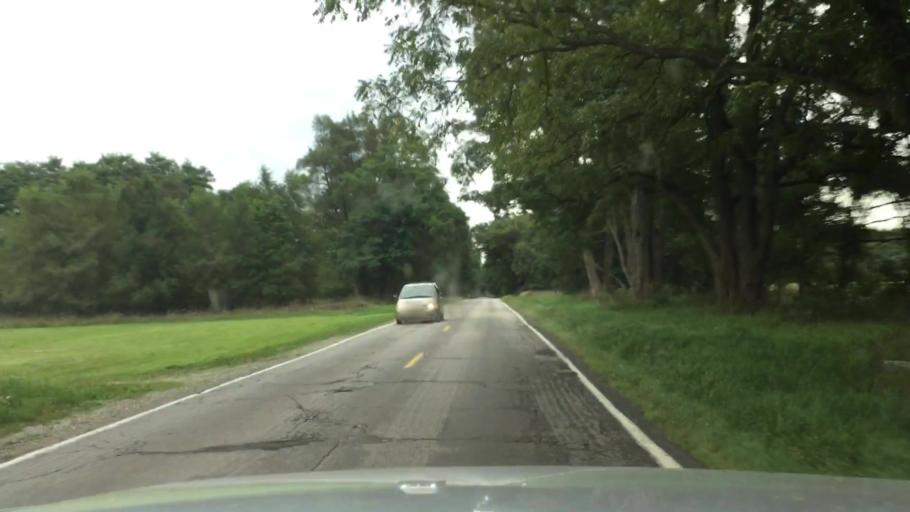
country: US
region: Michigan
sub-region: Genesee County
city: Argentine
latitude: 42.8141
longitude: -83.9088
